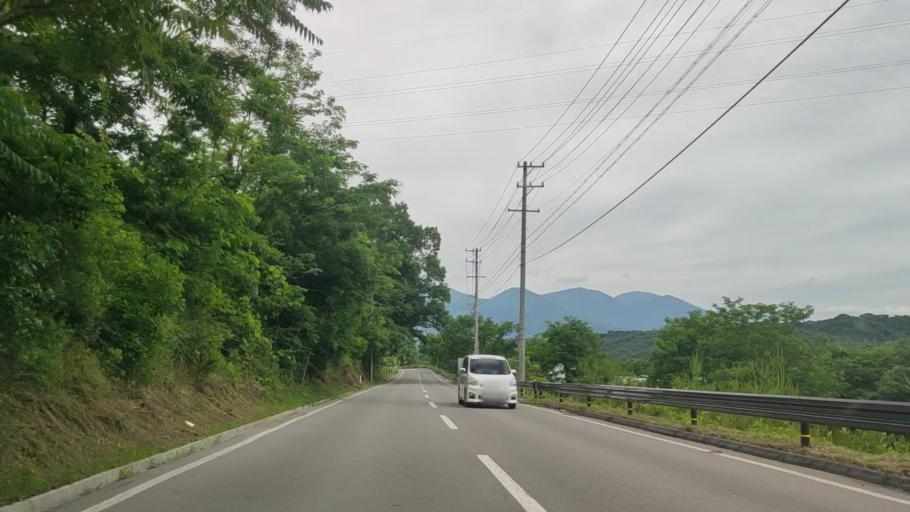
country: JP
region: Nagano
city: Kamimaruko
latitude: 36.3212
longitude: 138.3365
